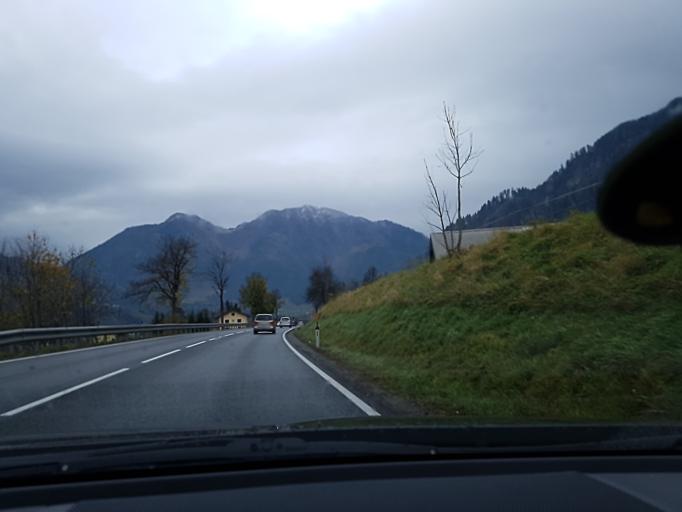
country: AT
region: Salzburg
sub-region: Politischer Bezirk Sankt Johann im Pongau
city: Sankt Johann im Pongau
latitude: 47.3469
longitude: 13.1937
